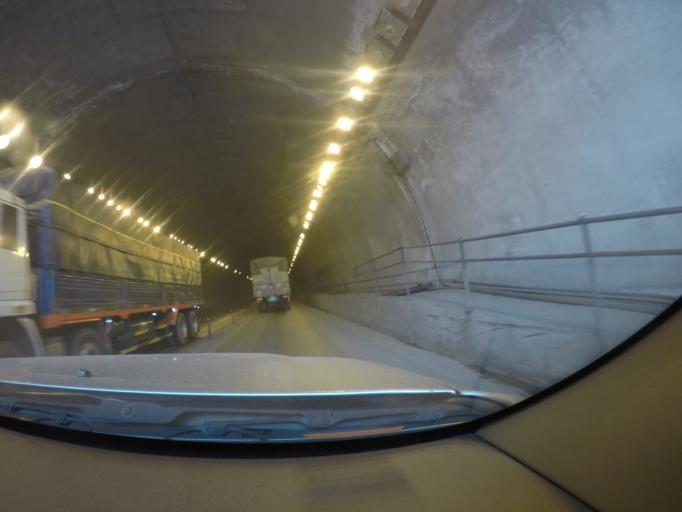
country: VN
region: Ha Tinh
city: Ky Anh
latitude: 17.9584
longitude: 106.4677
